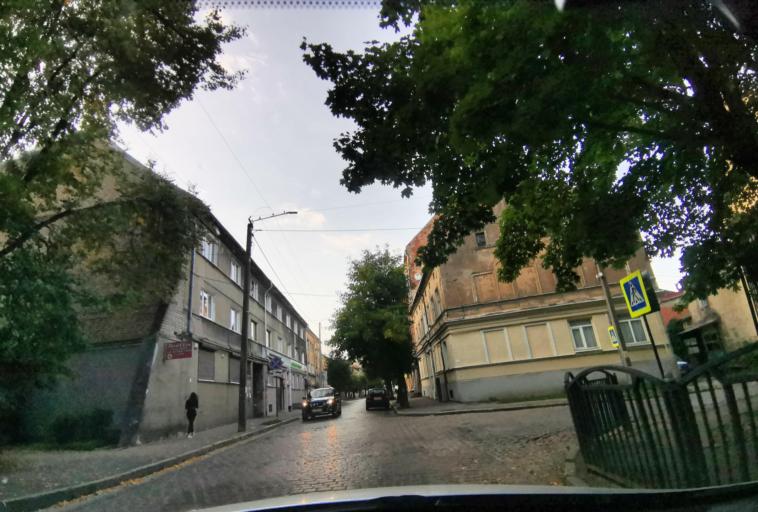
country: RU
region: Kaliningrad
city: Sovetsk
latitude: 55.0796
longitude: 21.8905
